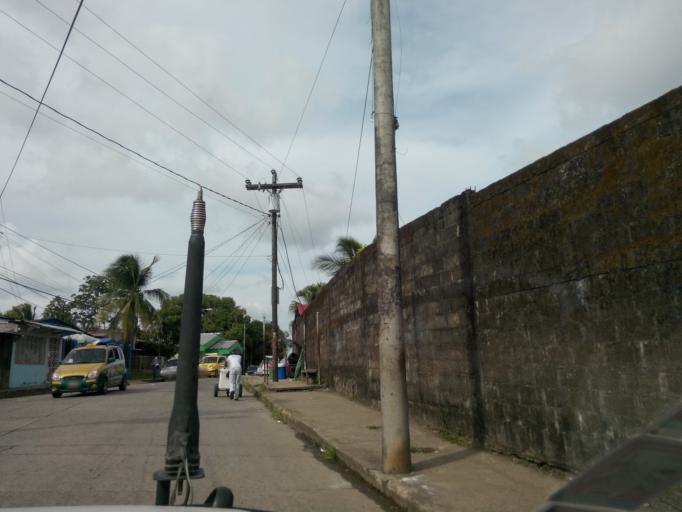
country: NI
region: Atlantico Sur
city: Bluefields
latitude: 12.0075
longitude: -83.7650
